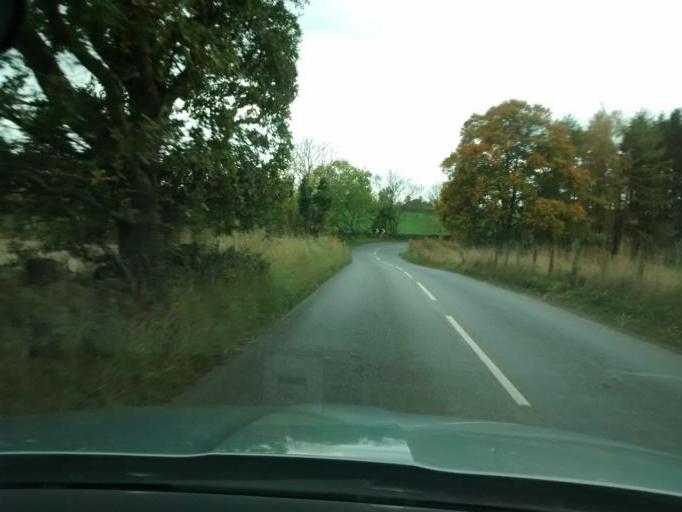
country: GB
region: Scotland
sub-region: Perth and Kinross
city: Stanley
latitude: 56.5012
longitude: -3.4278
